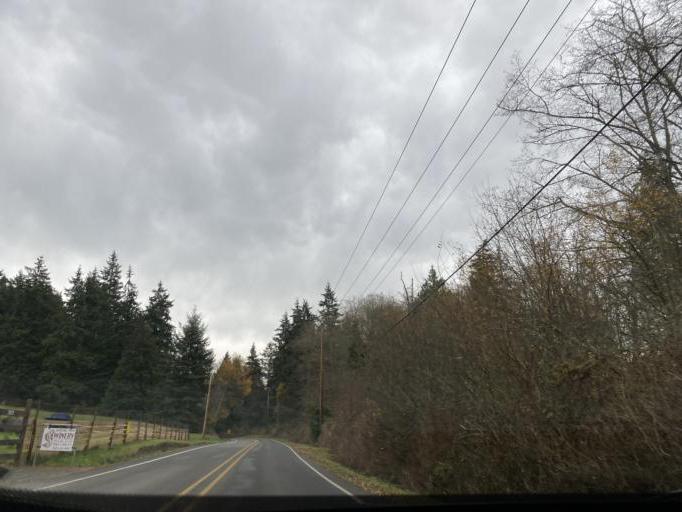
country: US
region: Washington
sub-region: Island County
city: Freeland
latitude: 48.0138
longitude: -122.5113
